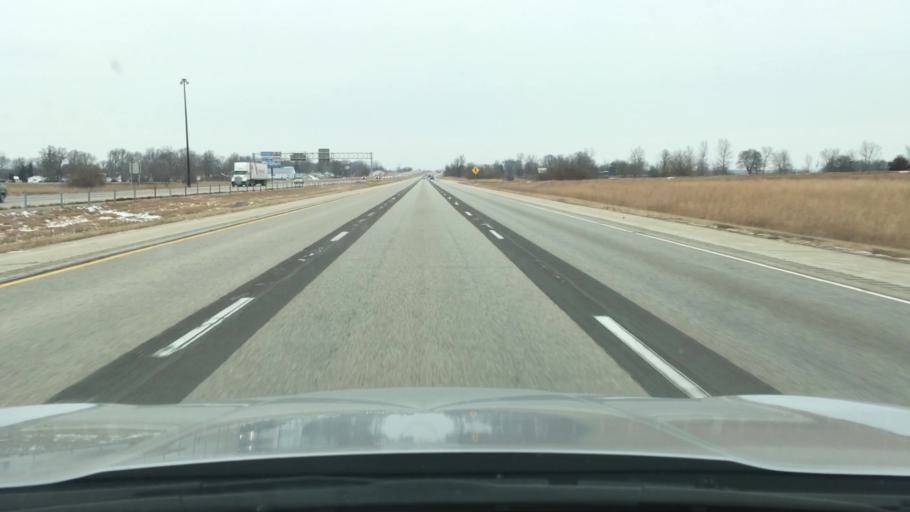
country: US
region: Illinois
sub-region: Sangamon County
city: Divernon
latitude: 39.6174
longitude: -89.6468
